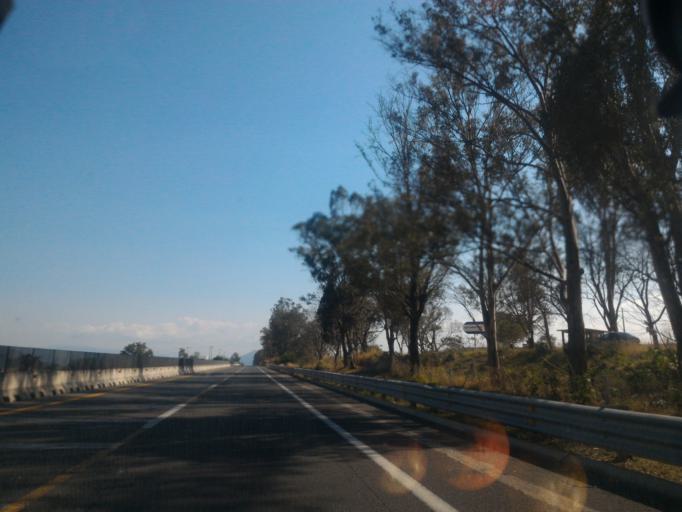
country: MX
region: Jalisco
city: Zapotiltic
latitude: 19.6135
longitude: -103.4596
